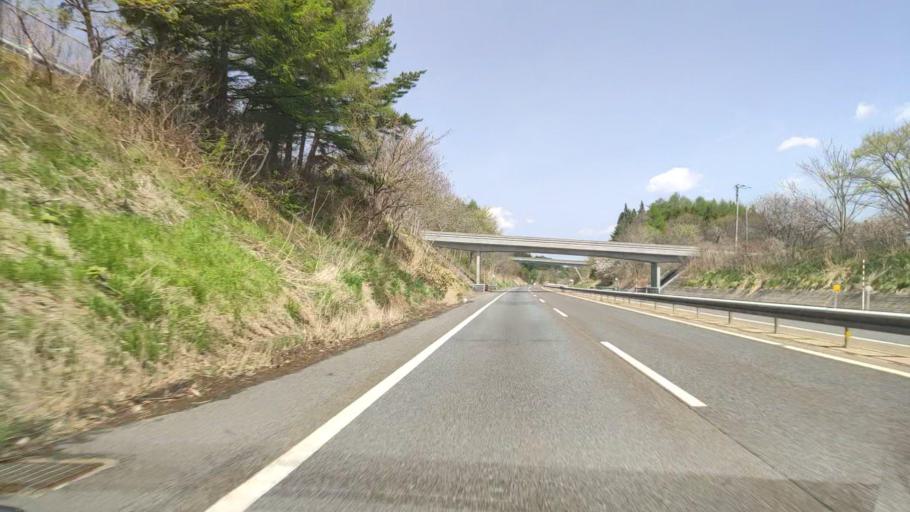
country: JP
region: Iwate
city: Ichinohe
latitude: 40.2596
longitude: 141.4014
